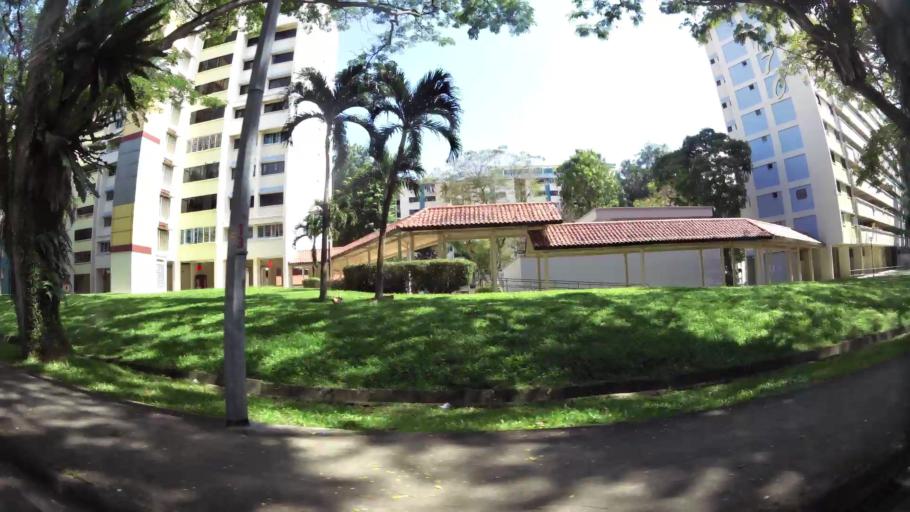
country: SG
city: Singapore
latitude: 1.3742
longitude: 103.8359
